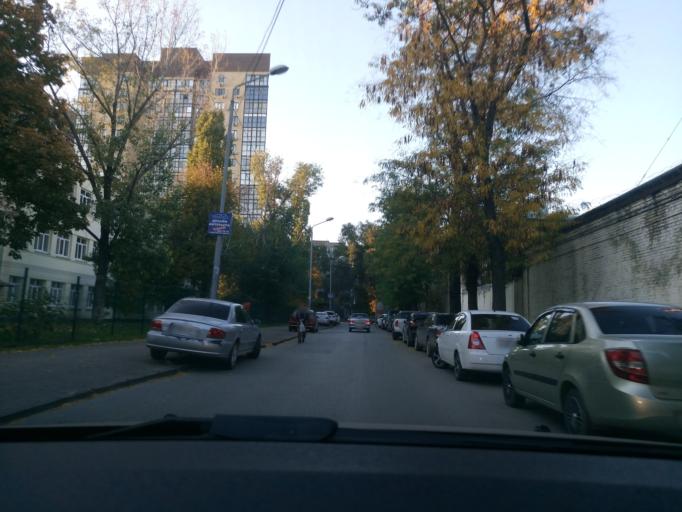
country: RU
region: Rostov
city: Rostov-na-Donu
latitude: 47.2340
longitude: 39.6984
